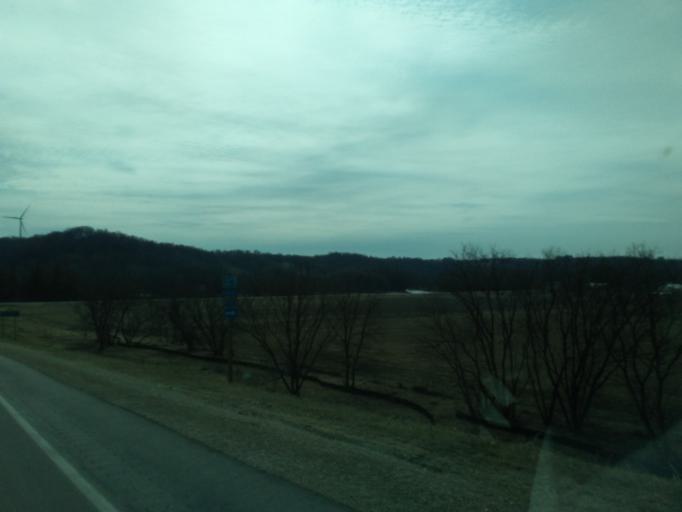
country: US
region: Iowa
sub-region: Winneshiek County
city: Decorah
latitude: 43.3236
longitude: -91.8135
